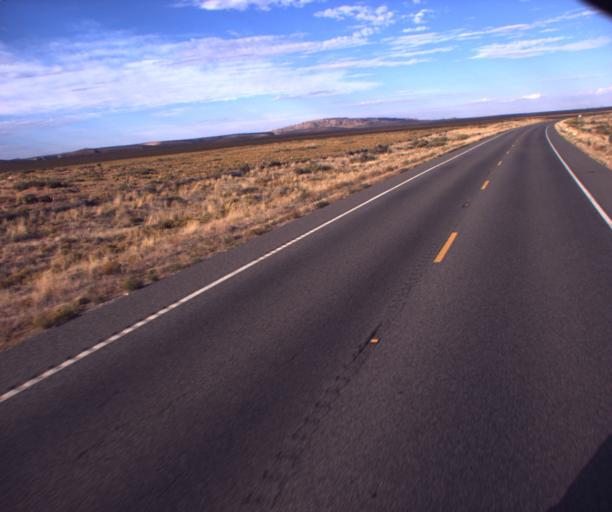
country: US
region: Arizona
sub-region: Apache County
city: Lukachukai
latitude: 36.9298
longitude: -109.2139
